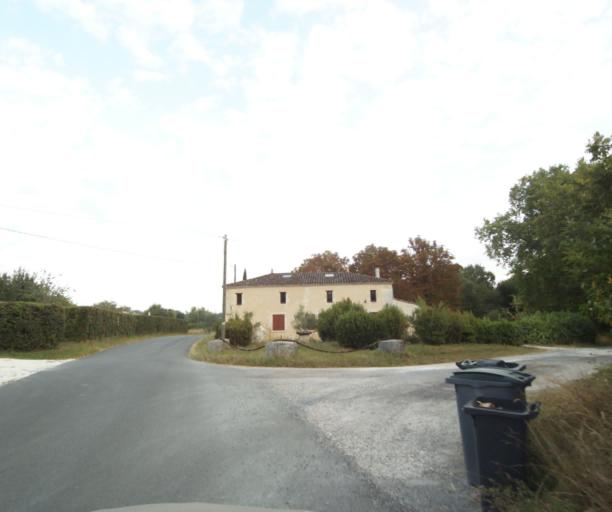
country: FR
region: Aquitaine
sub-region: Departement de la Gironde
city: La Sauve
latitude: 44.7892
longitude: -0.3262
